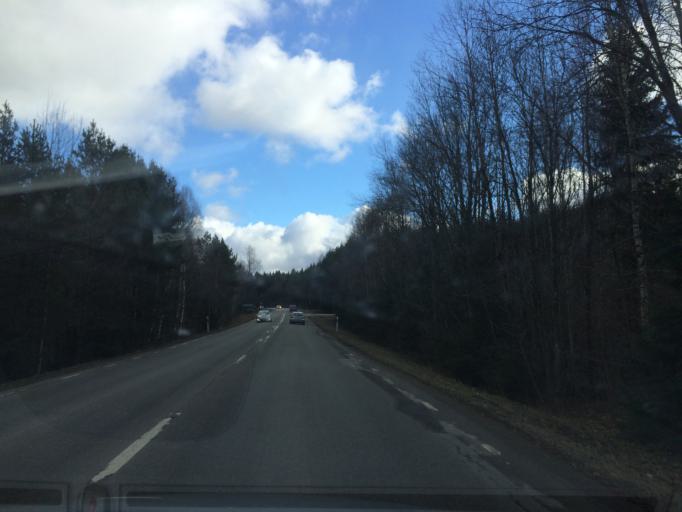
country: SE
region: Vaestra Goetaland
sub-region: Skara Kommun
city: Skara
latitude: 58.3143
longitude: 13.4440
